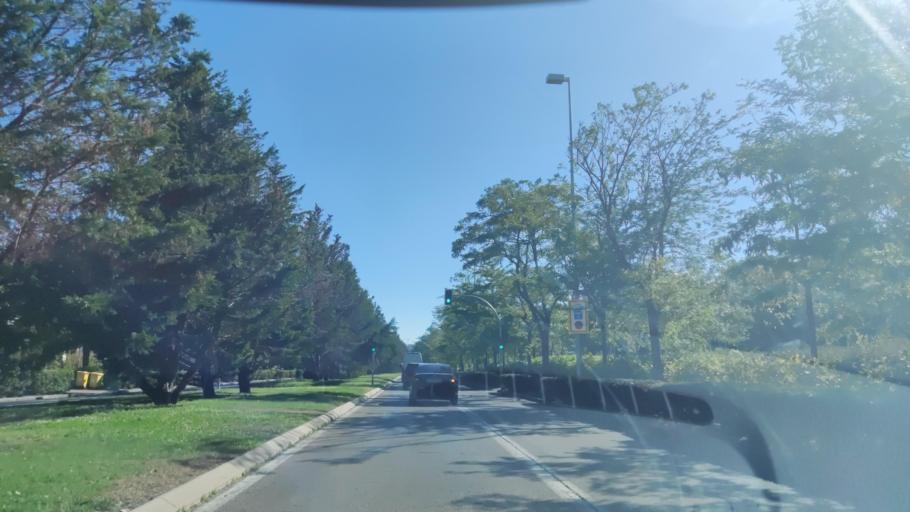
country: ES
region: Madrid
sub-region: Provincia de Madrid
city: Carabanchel
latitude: 40.3819
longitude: -3.7241
